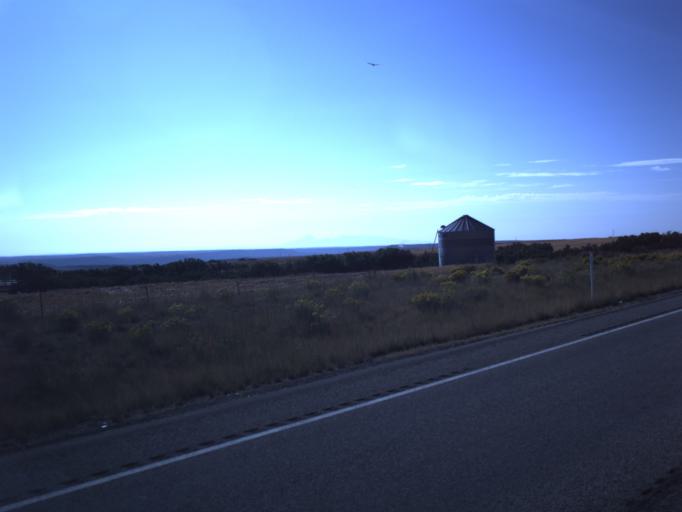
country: US
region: Utah
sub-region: San Juan County
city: Monticello
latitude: 37.8402
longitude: -109.3369
